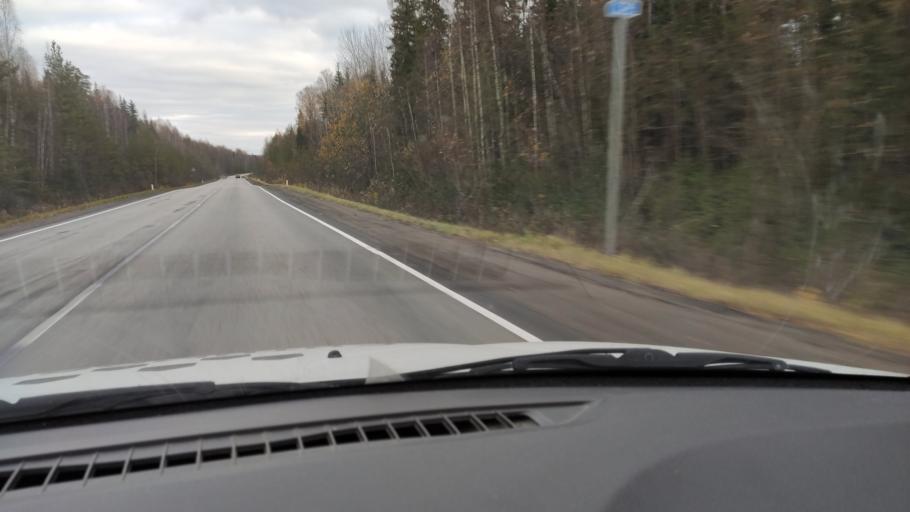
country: RU
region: Kirov
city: Chernaya Kholunitsa
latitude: 58.8689
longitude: 51.5536
